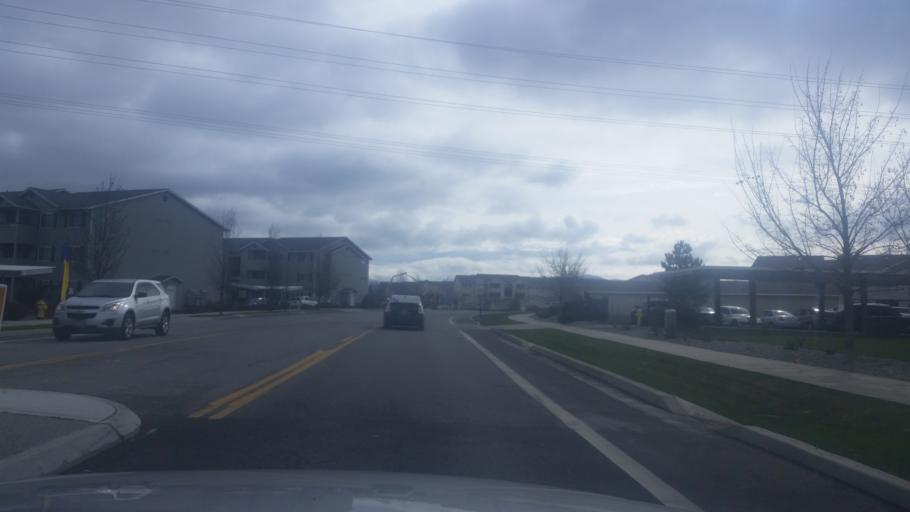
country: US
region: Washington
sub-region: Spokane County
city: Spokane Valley
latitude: 47.6775
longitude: -117.2353
